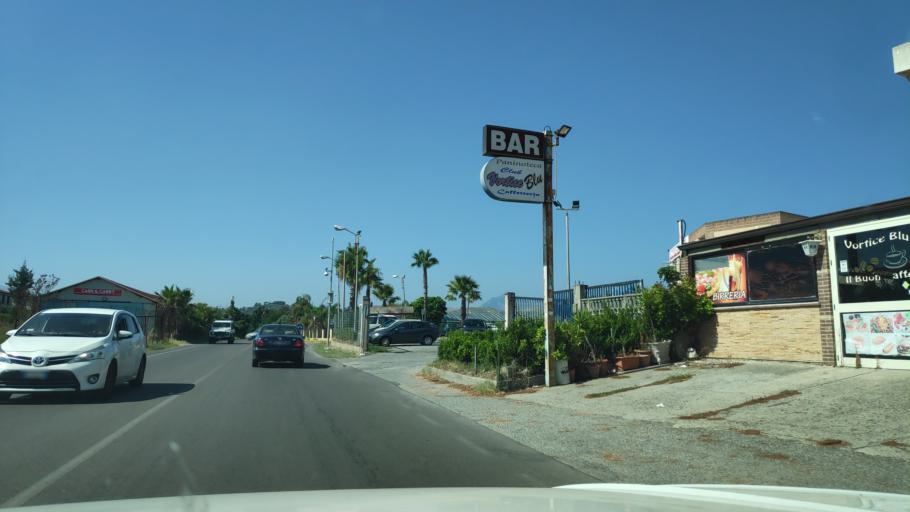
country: IT
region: Calabria
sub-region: Provincia di Reggio Calabria
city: Bovalino
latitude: 38.1336
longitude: 16.1622
